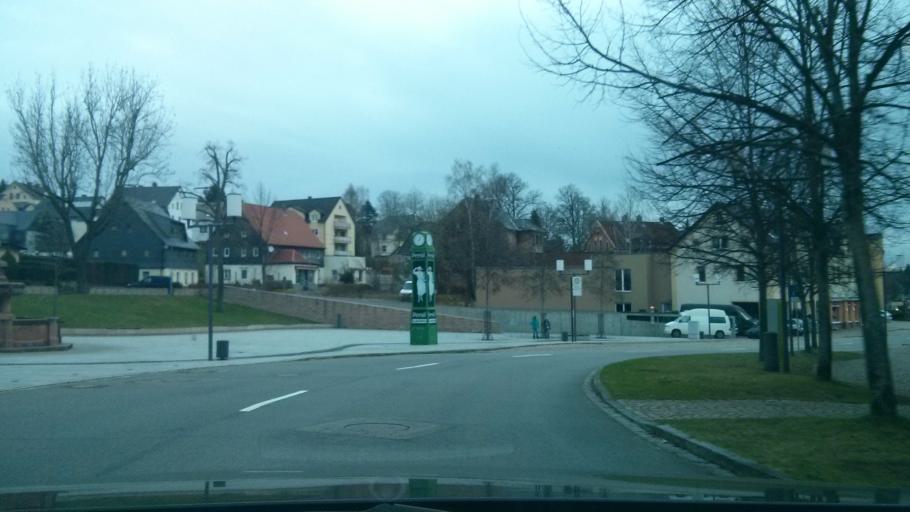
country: DE
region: Saxony
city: Oelsnitz
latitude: 50.7223
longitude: 12.6985
